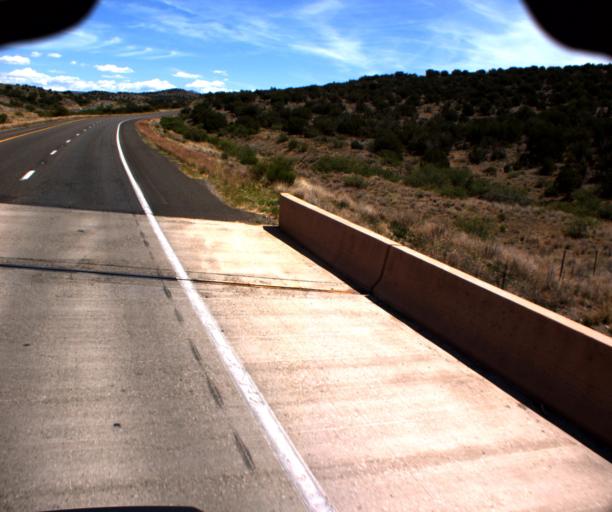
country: US
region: Arizona
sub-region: Yavapai County
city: Cornville
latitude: 34.7837
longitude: -111.9242
